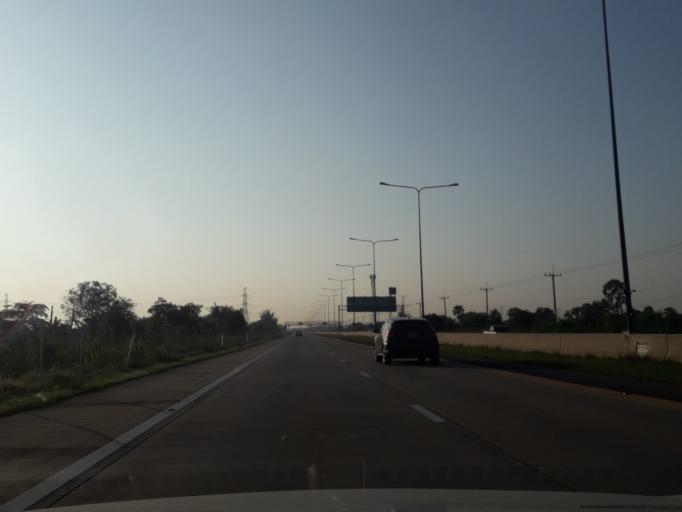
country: TH
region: Pathum Thani
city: Sam Khok
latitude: 14.1383
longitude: 100.5623
